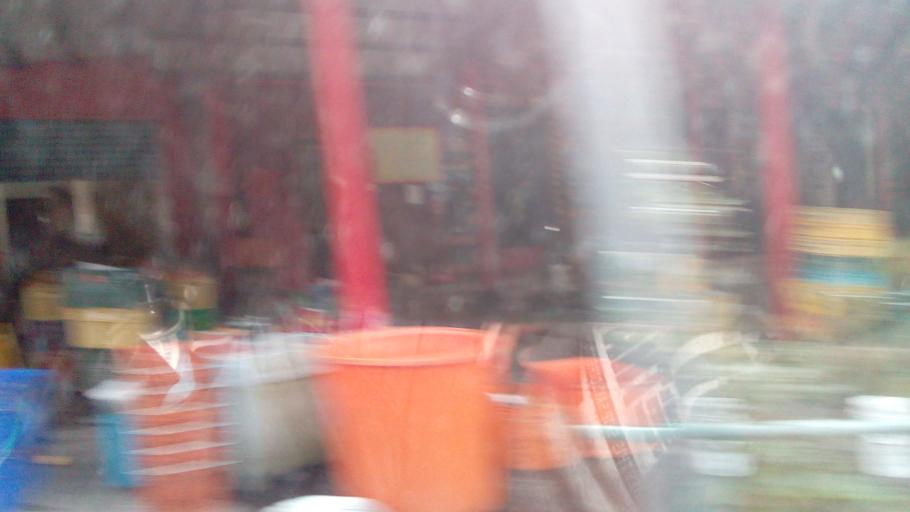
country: TW
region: Taiwan
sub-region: Hualien
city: Hualian
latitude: 24.3553
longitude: 121.3253
